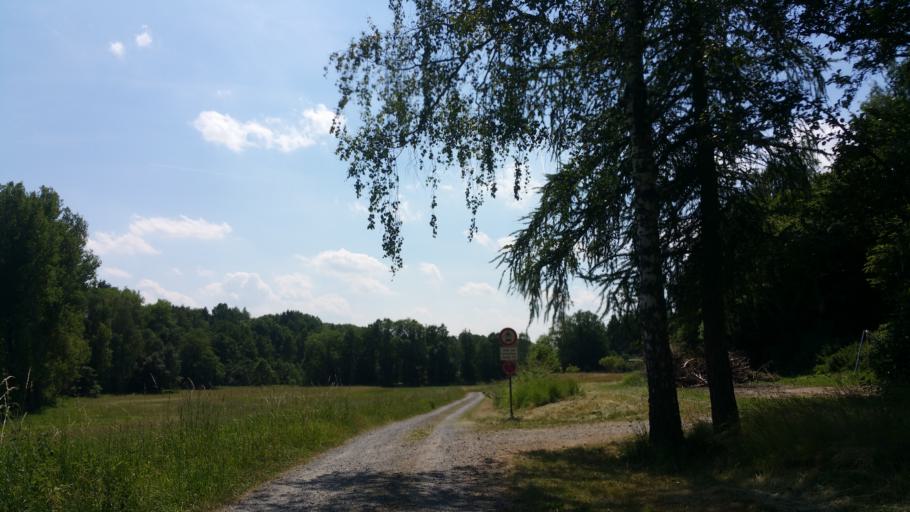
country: DE
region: Bavaria
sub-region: Upper Franconia
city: Schwarzenbach an der Saale
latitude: 50.2173
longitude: 11.9272
